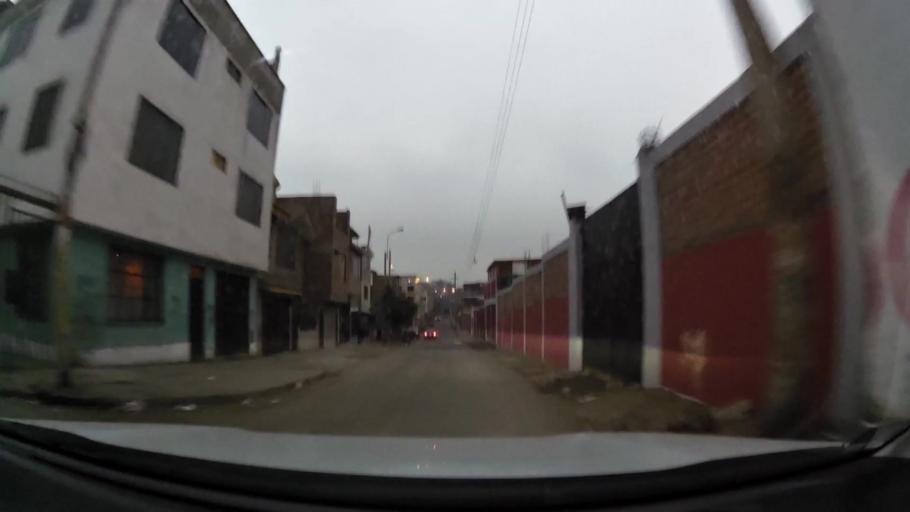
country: PE
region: Lima
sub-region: Lima
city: Surco
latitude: -12.1457
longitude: -76.9752
